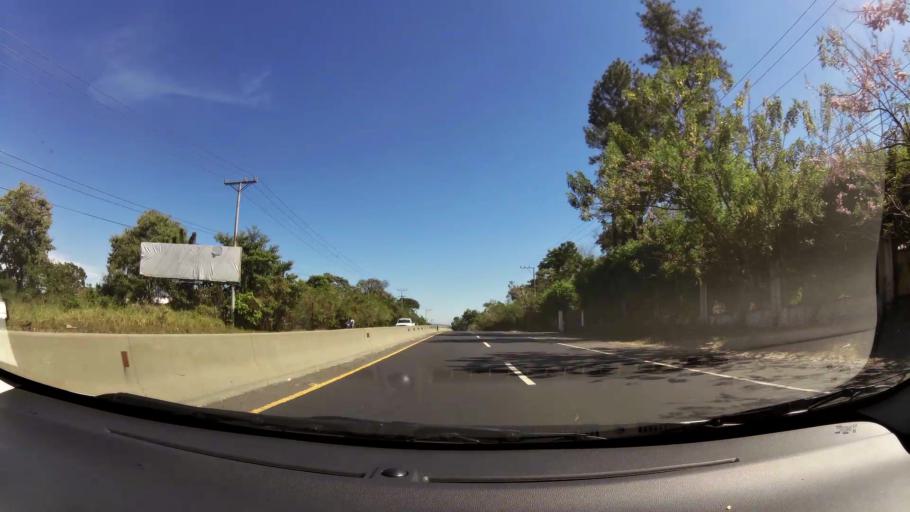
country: SV
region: La Libertad
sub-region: Distrito de Quezaltepeque
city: Quezaltepeque
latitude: 13.8194
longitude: -89.2954
